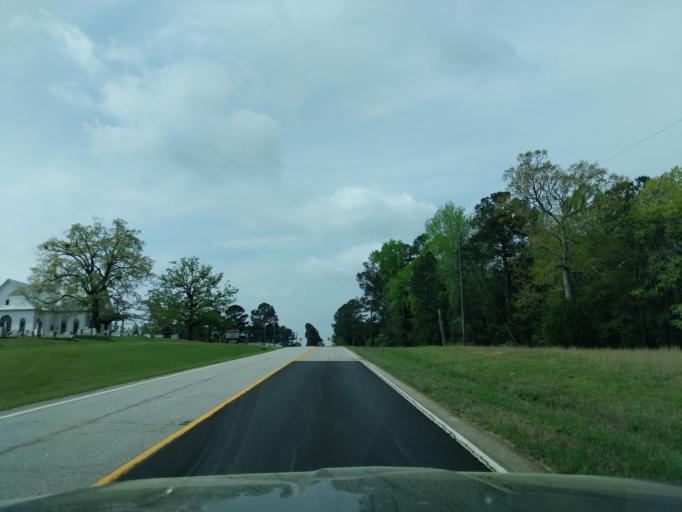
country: US
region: Georgia
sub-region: Lincoln County
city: Lincolnton
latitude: 33.7529
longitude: -82.3879
